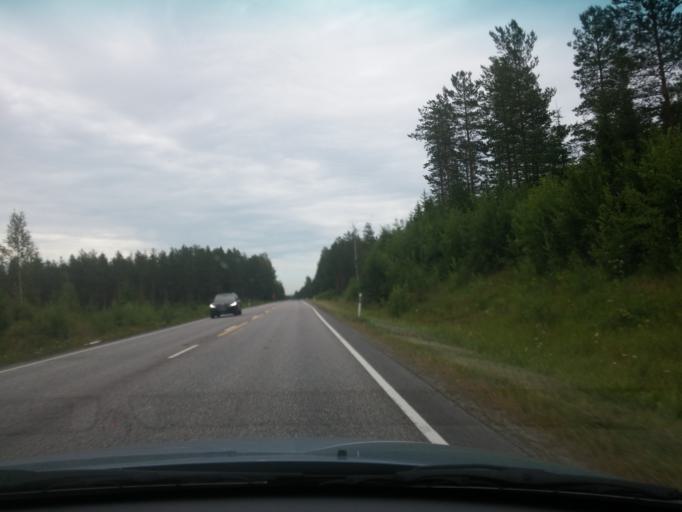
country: FI
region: Haeme
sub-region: Riihimaeki
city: Loppi
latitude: 60.7243
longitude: 24.4192
